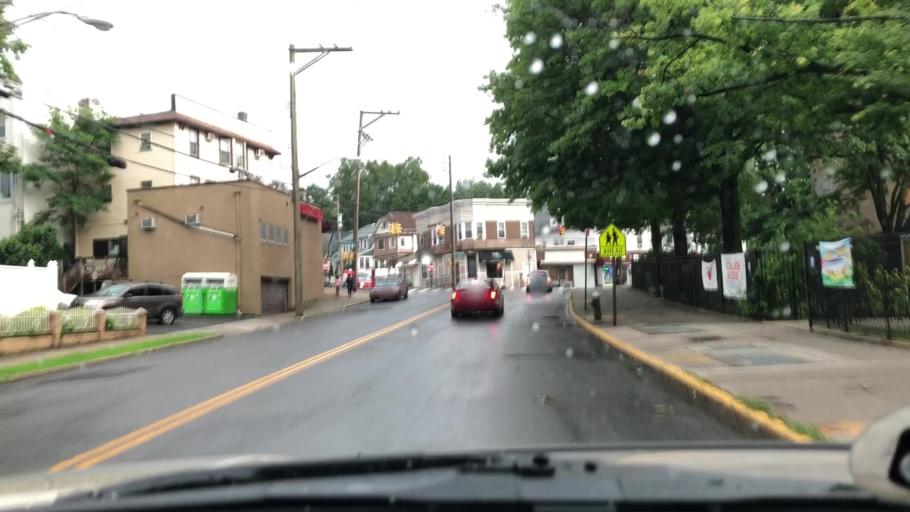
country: US
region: New Jersey
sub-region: Hudson County
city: Bayonne
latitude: 40.6345
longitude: -74.0970
